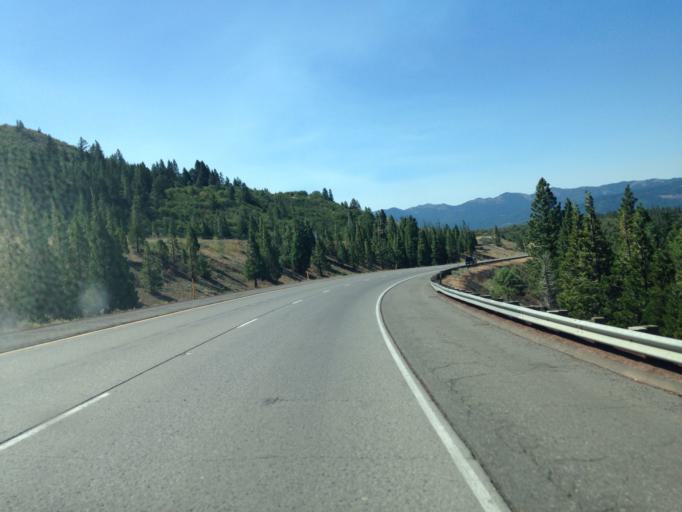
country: US
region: Oregon
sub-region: Jackson County
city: Ashland
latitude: 42.0388
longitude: -122.5990
